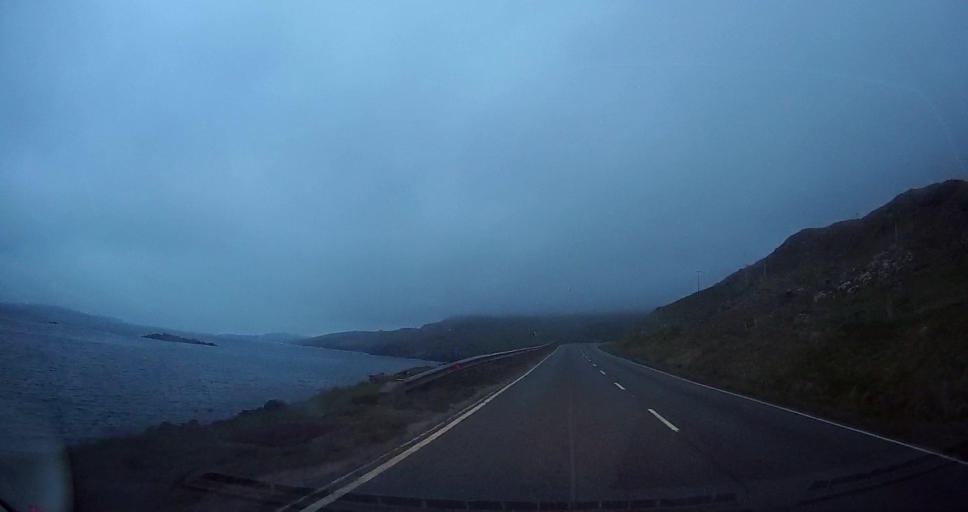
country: GB
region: Scotland
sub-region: Shetland Islands
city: Sandwick
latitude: 60.0338
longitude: -1.2333
